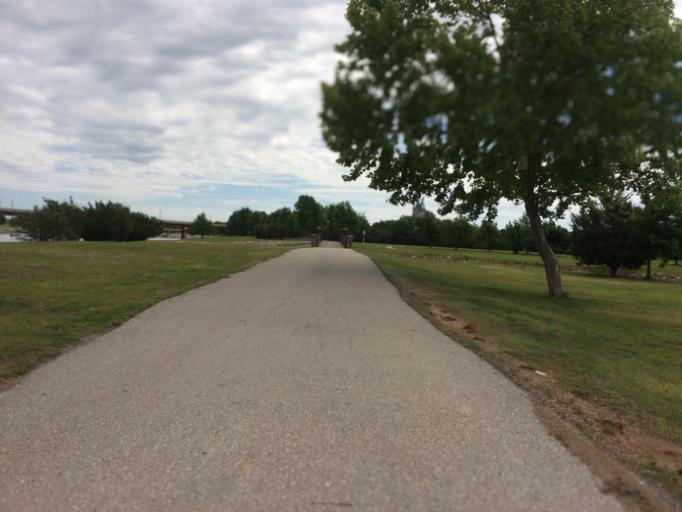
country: US
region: Oklahoma
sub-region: Oklahoma County
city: Oklahoma City
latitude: 35.4481
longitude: -97.5245
